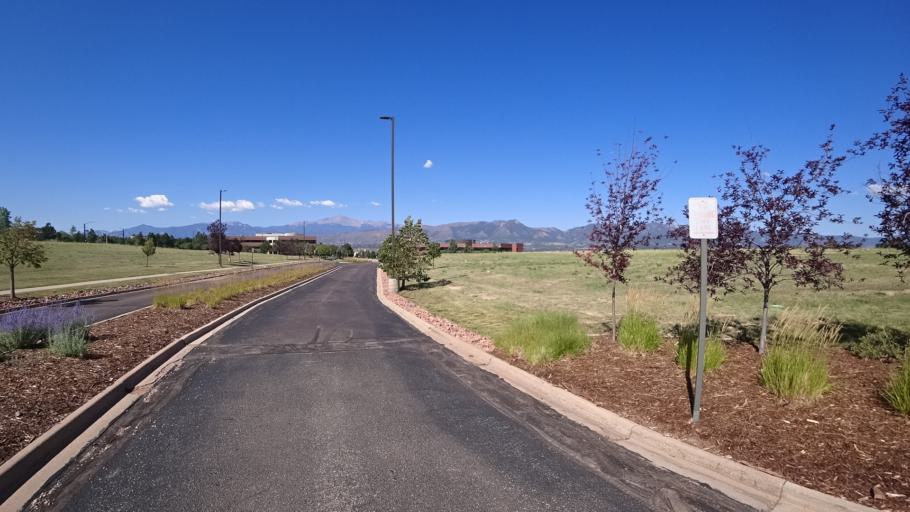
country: US
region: Colorado
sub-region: El Paso County
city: Air Force Academy
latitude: 38.9676
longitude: -104.7880
